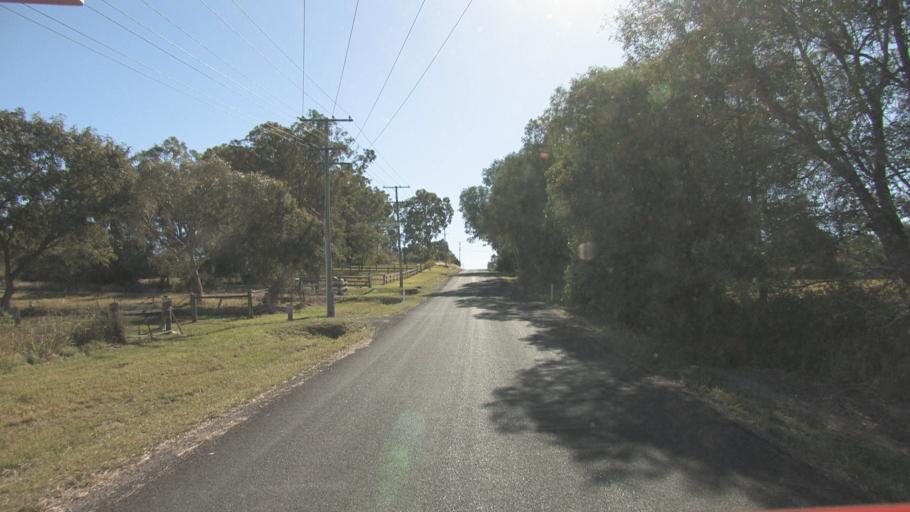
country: AU
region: Queensland
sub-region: Logan
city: Chambers Flat
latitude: -27.7587
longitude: 153.0691
